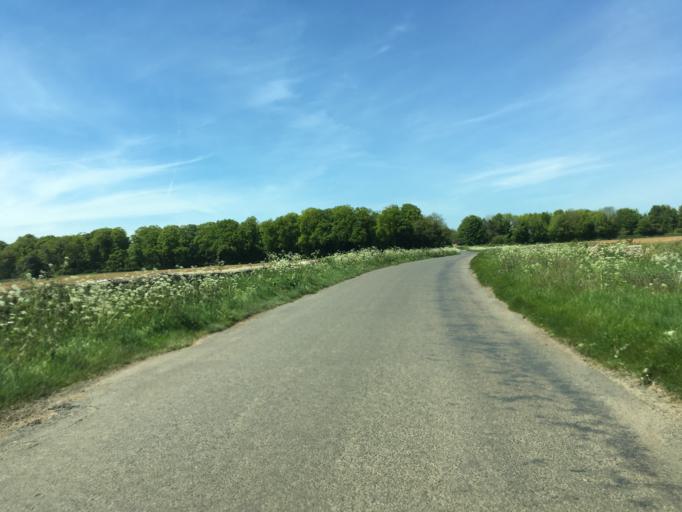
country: GB
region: England
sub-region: Gloucestershire
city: Coates
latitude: 51.6912
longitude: -2.0130
